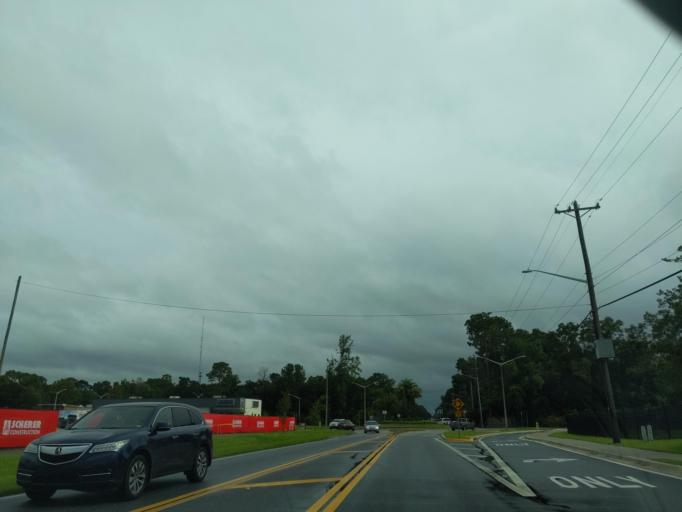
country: US
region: Florida
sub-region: Alachua County
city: Gainesville
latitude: 29.6390
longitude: -82.4225
